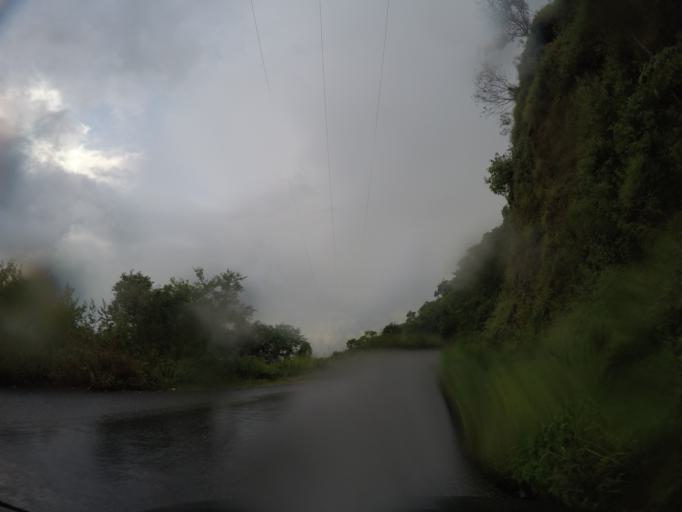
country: MX
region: Oaxaca
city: San Gabriel Mixtepec
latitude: 16.0627
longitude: -97.0756
